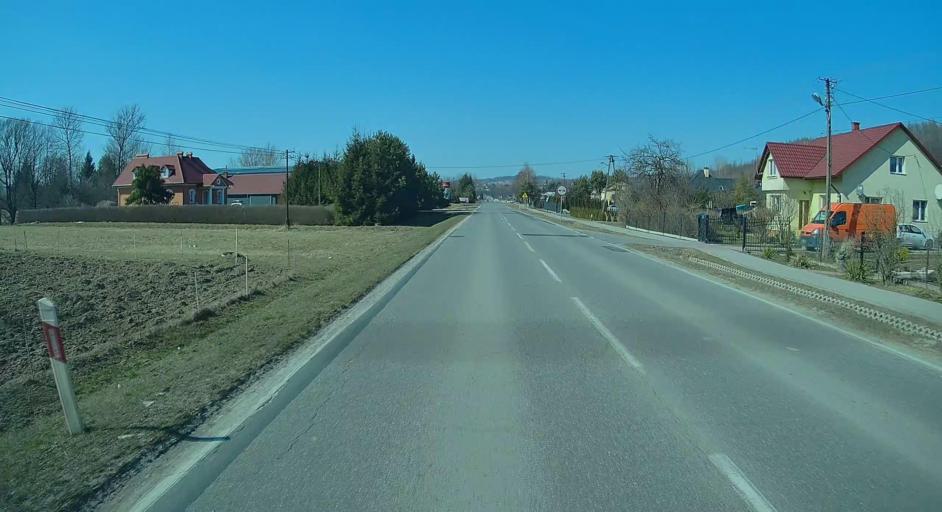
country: PL
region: Subcarpathian Voivodeship
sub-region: Powiat rzeszowski
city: Tyczyn
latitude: 49.9628
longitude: 22.0872
